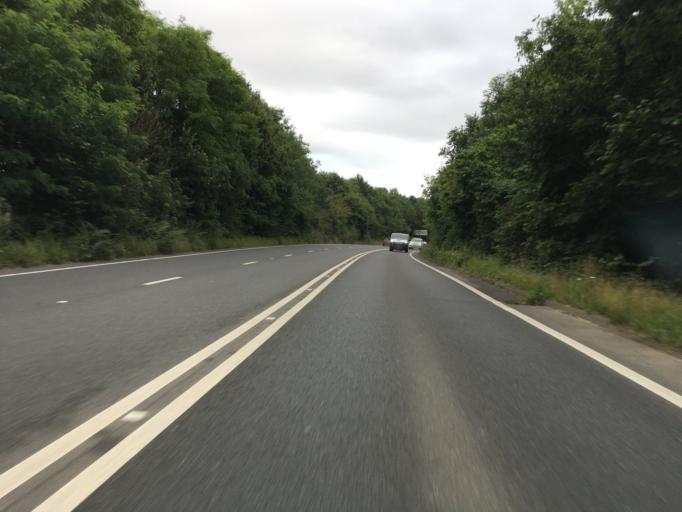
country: GB
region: England
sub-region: Hampshire
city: Petersfield
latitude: 51.0144
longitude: -0.9249
